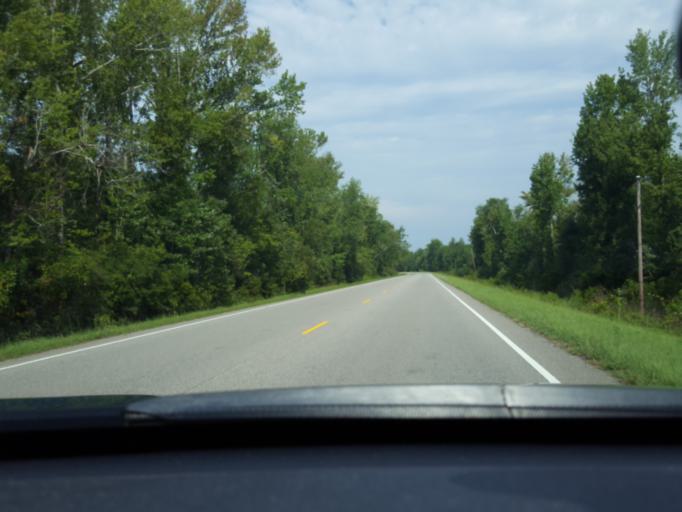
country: US
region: North Carolina
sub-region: Washington County
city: Plymouth
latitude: 35.9066
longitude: -76.7143
